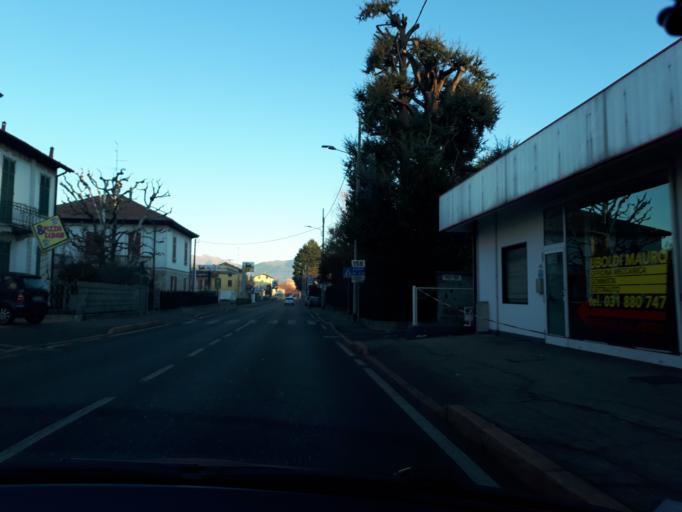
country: IT
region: Lombardy
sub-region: Provincia di Como
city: Fino Mornasco
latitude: 45.7515
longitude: 9.0505
